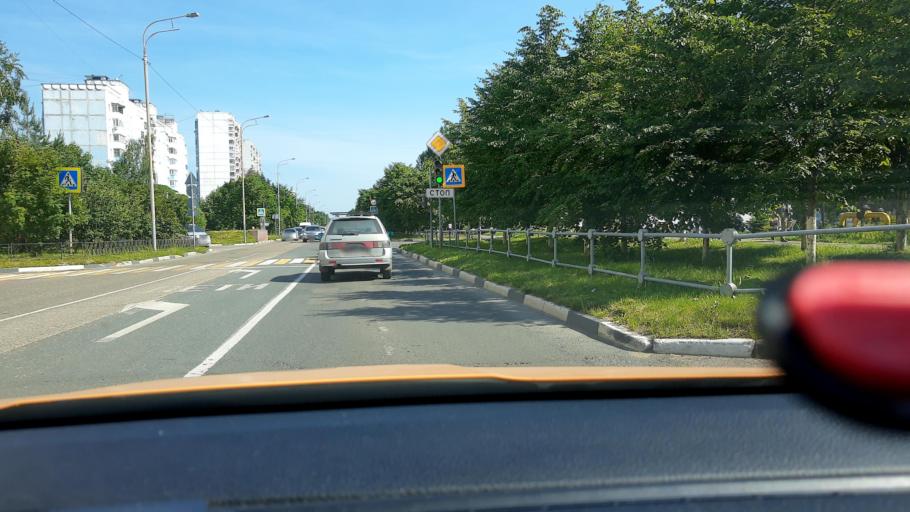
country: RU
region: Moskovskaya
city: Krasnoznamensk
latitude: 55.5922
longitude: 37.0353
